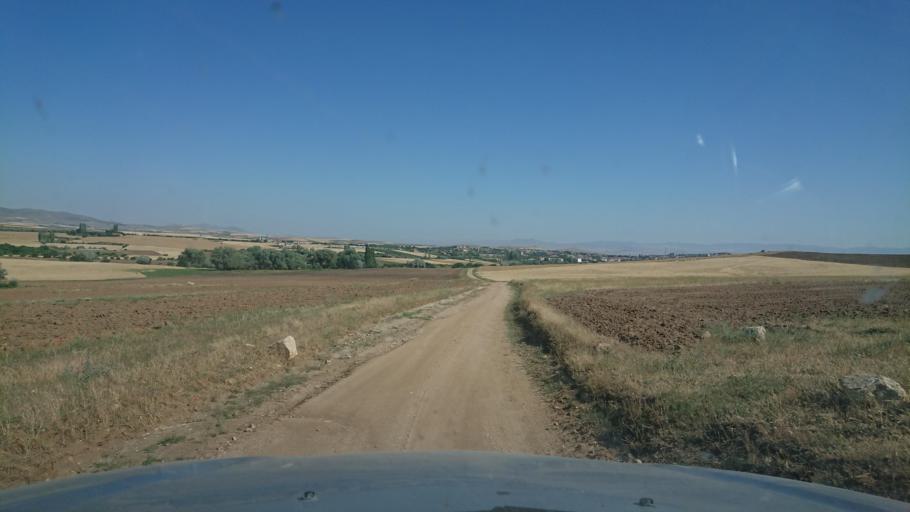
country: TR
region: Aksaray
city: Agacoren
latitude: 38.8492
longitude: 33.9162
